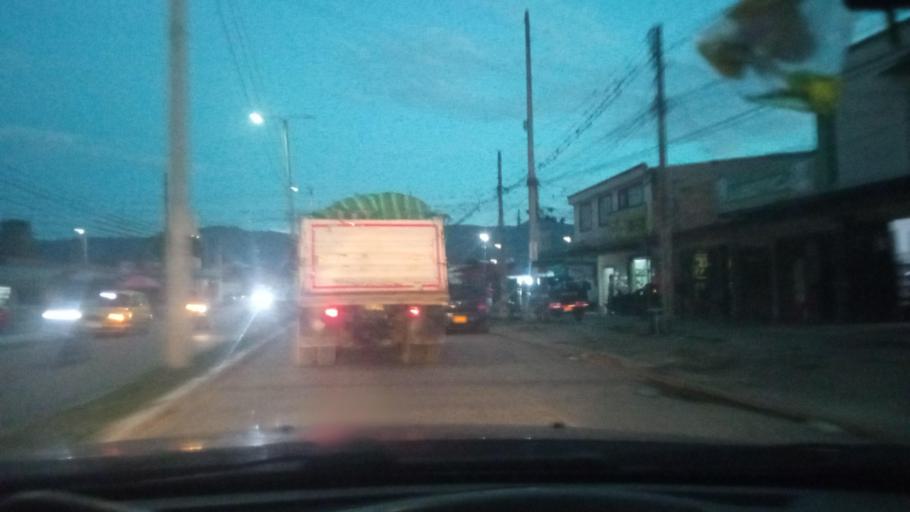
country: CO
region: Huila
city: Pitalito
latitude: 1.8572
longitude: -76.0468
